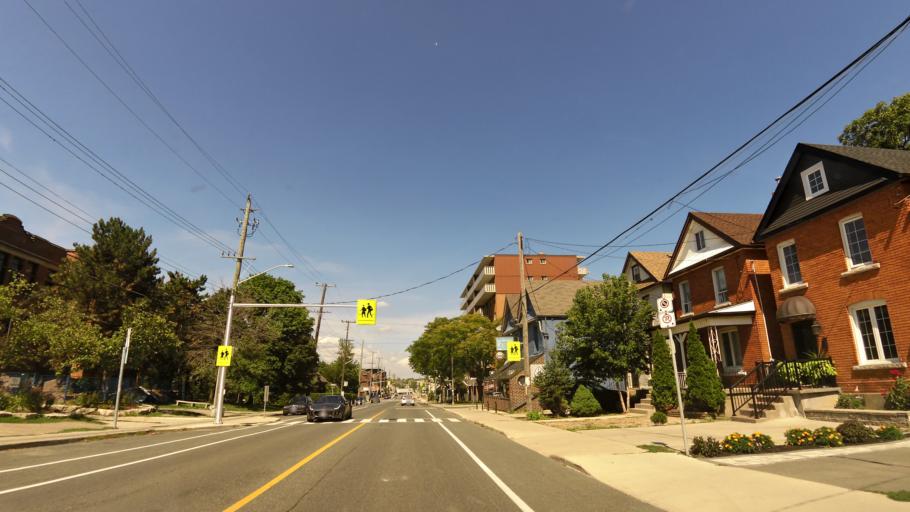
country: CA
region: Ontario
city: Hamilton
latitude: 43.2514
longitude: -79.8923
